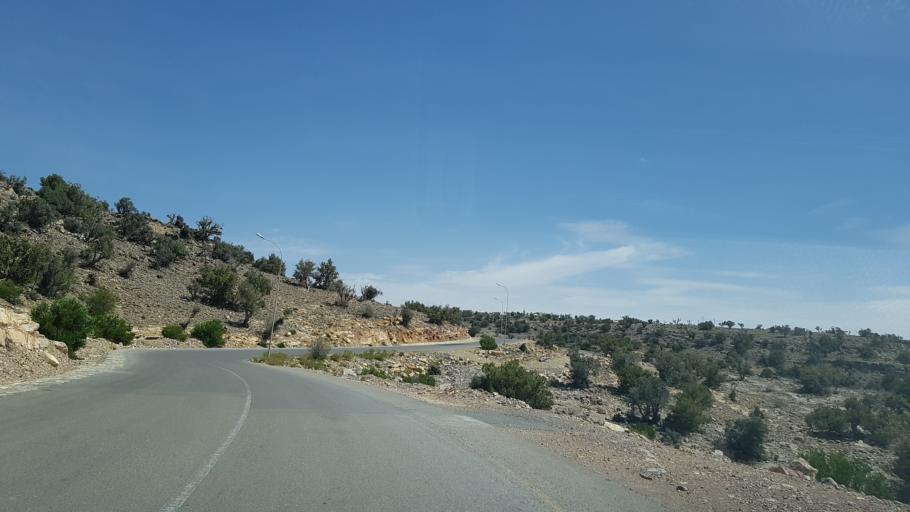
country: OM
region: Al Batinah
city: Bayt al `Awabi
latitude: 23.1388
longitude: 57.5944
